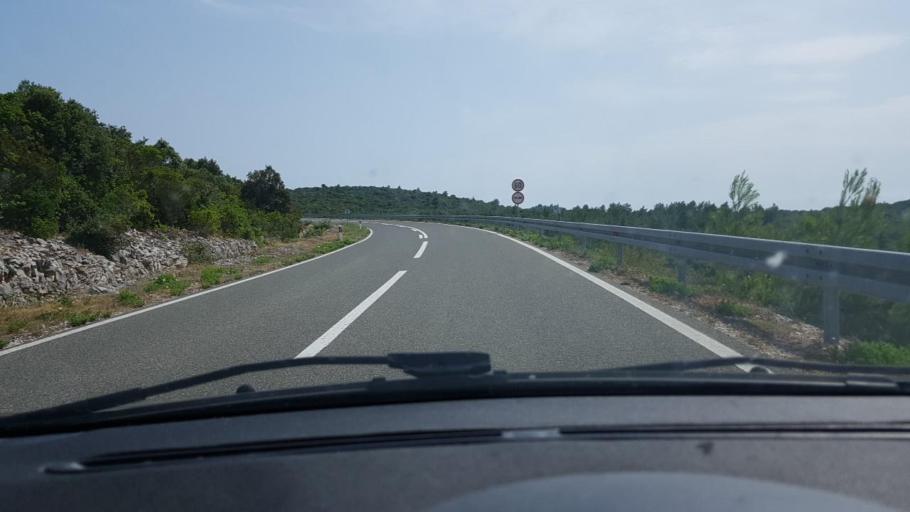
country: HR
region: Dubrovacko-Neretvanska
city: Smokvica
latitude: 42.9517
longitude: 16.9419
